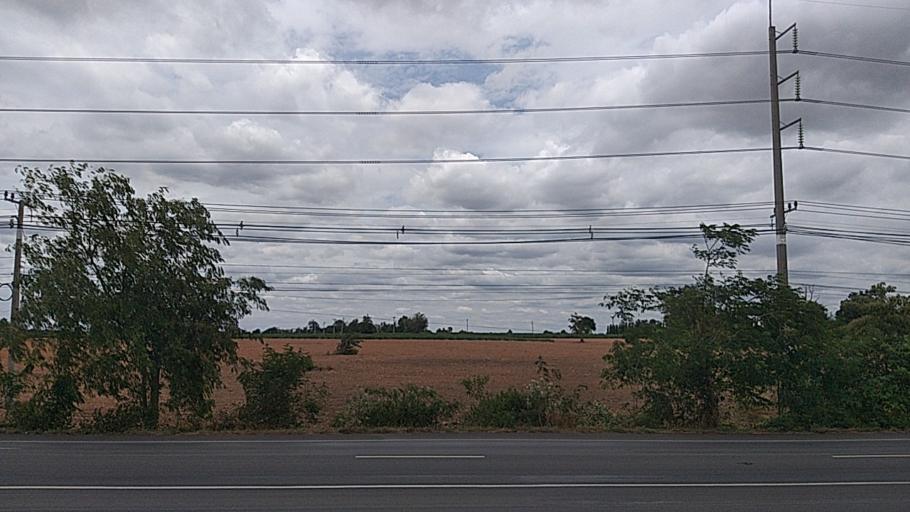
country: TH
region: Nakhon Ratchasima
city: Chok Chai
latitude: 14.7376
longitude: 102.0954
